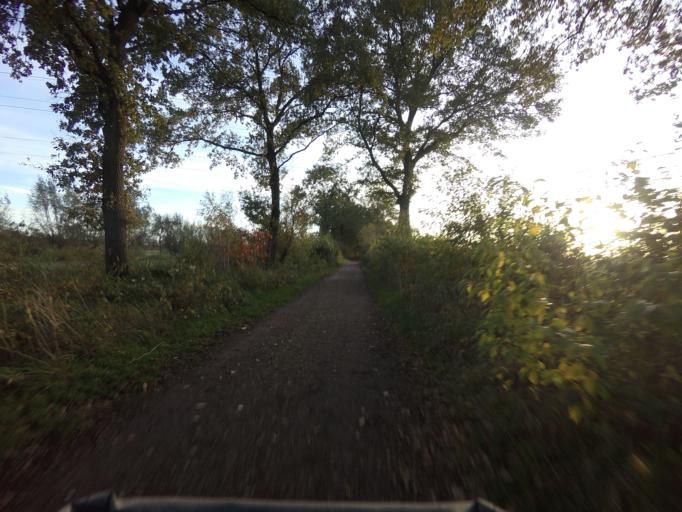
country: NL
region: Utrecht
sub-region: Gemeente De Bilt
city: De Bilt
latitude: 52.1488
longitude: 5.1783
